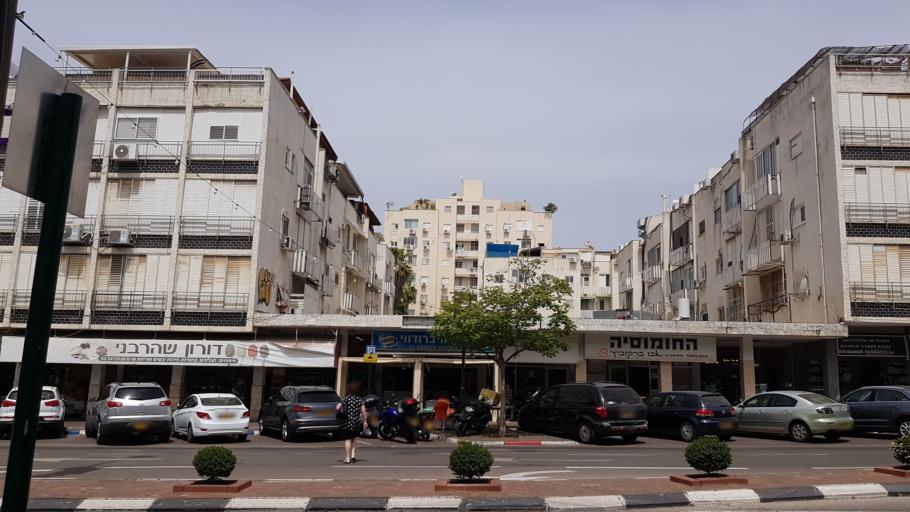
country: IL
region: Tel Aviv
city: Ramat HaSharon
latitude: 32.1390
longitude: 34.8421
